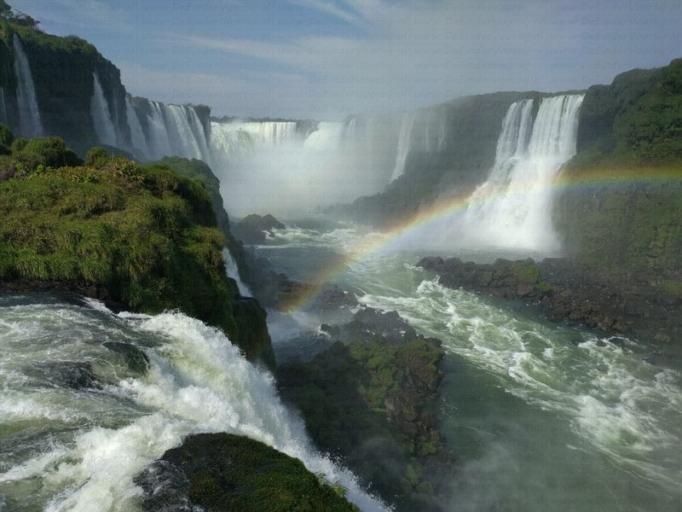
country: AR
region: Misiones
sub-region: Departamento de Iguazu
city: Puerto Iguazu
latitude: -25.6919
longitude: -54.4380
